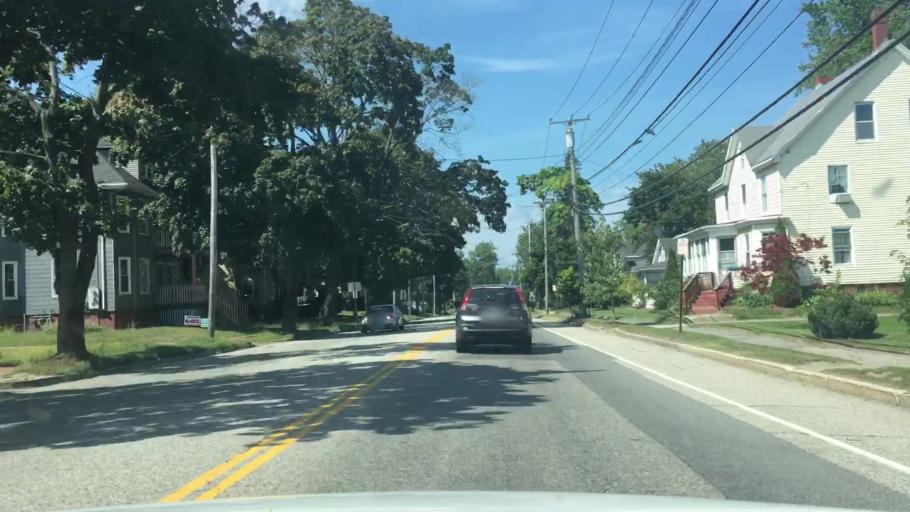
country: US
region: Maine
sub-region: Cumberland County
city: Portland
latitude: 43.6863
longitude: -70.2691
